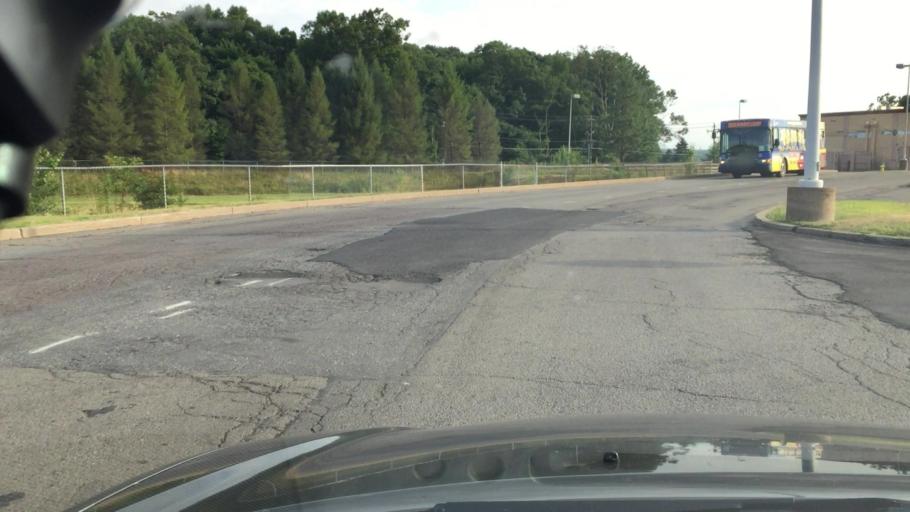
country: US
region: Pennsylvania
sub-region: Luzerne County
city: West Hazleton
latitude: 40.9830
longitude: -76.0141
